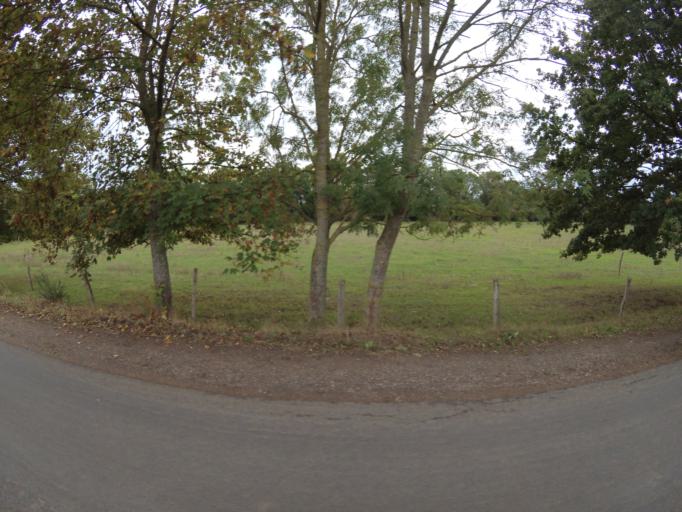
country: FR
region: Ile-de-France
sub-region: Departement de Seine-et-Marne
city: Gouvernes
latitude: 48.8604
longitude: 2.6830
